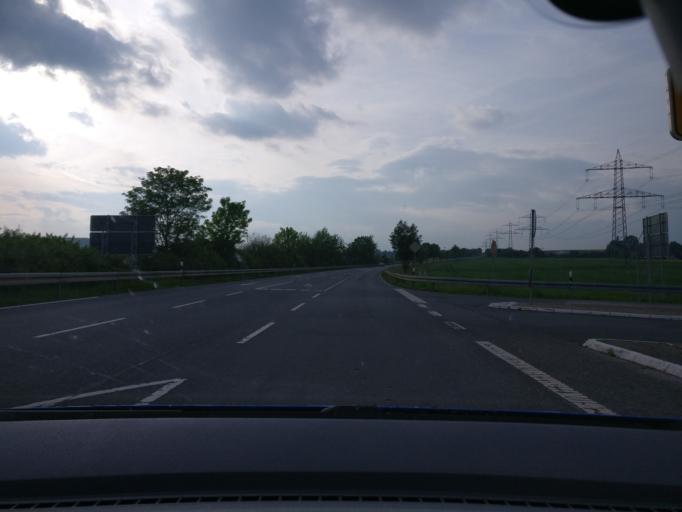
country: DE
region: Rheinland-Pfalz
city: Netzbach
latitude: 50.3378
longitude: 8.1266
